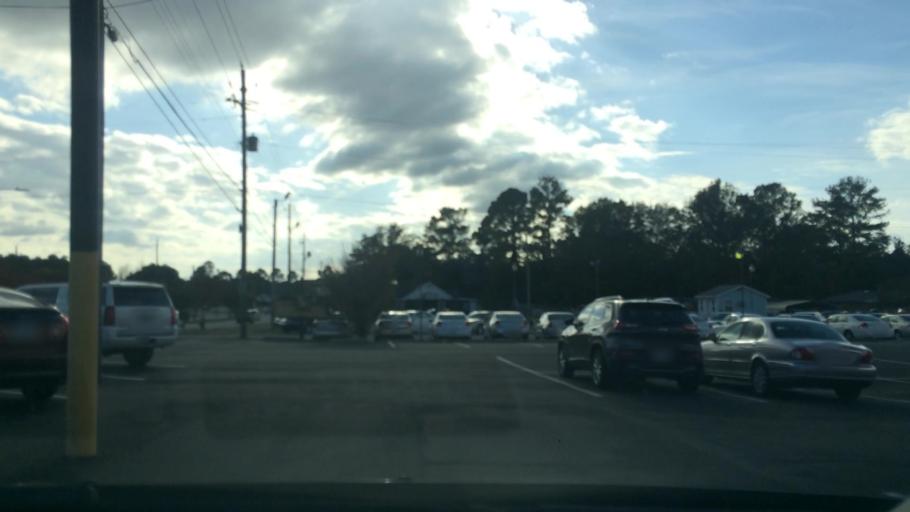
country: US
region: North Carolina
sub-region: Wayne County
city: Goldsboro
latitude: 35.3706
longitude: -77.9543
